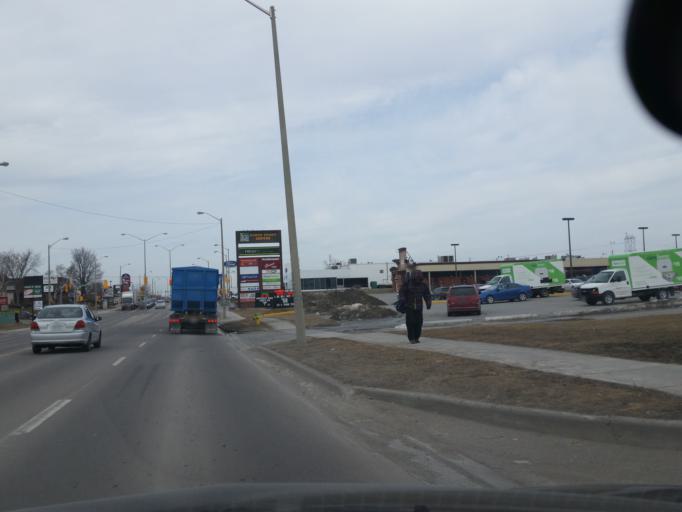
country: CA
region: Ontario
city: Belleville
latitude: 44.1840
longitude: -77.3941
